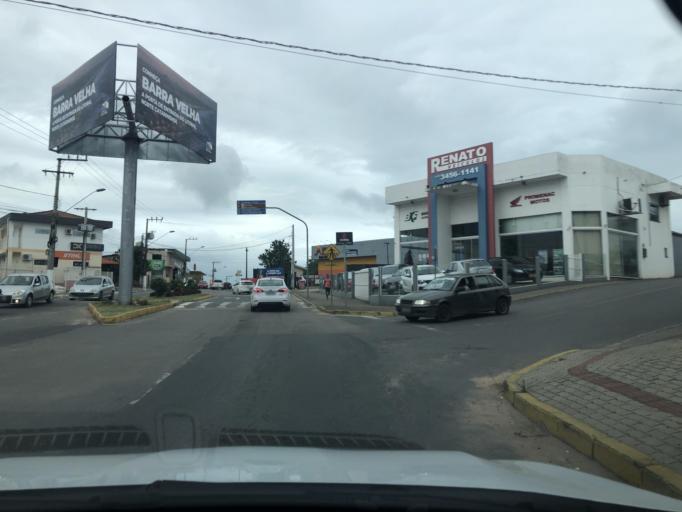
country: BR
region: Santa Catarina
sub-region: Barra Velha
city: Barra Velha
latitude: -26.6390
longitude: -48.6930
